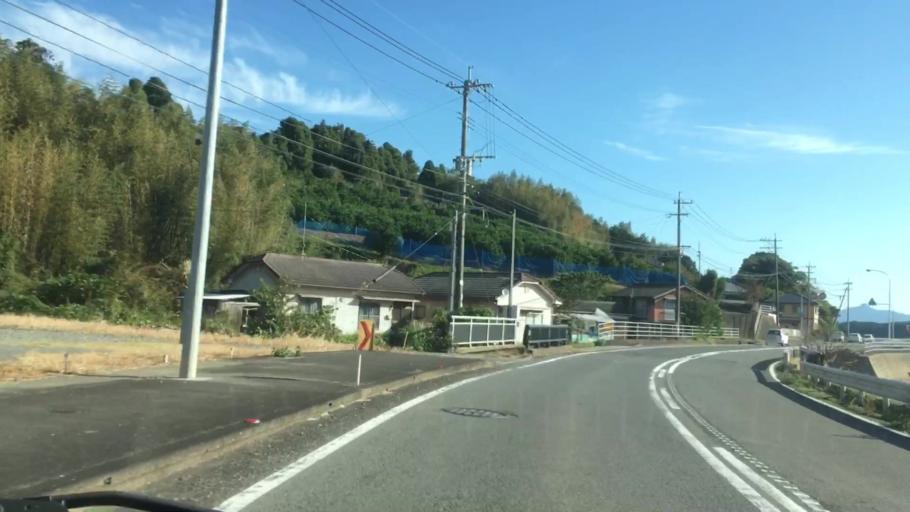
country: JP
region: Nagasaki
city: Sasebo
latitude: 33.0281
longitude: 129.7409
